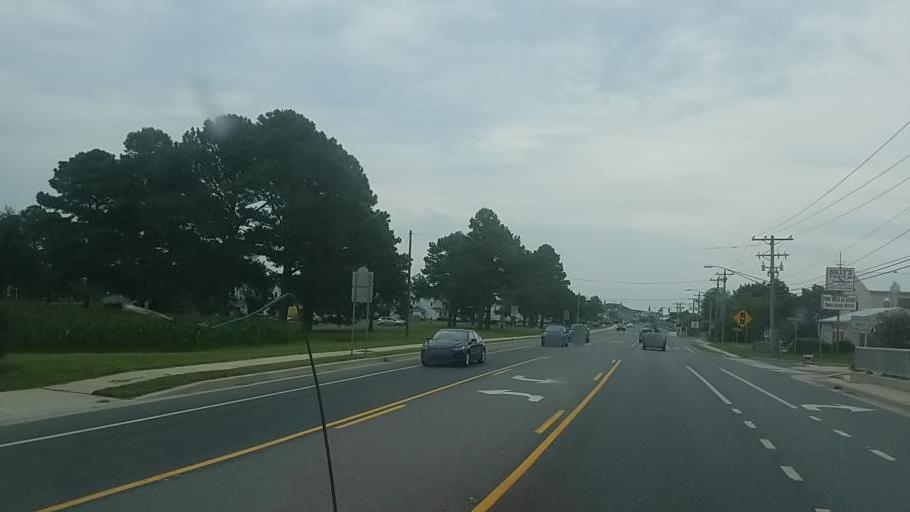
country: US
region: Delaware
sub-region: Sussex County
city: Ocean View
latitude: 38.4670
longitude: -75.0887
